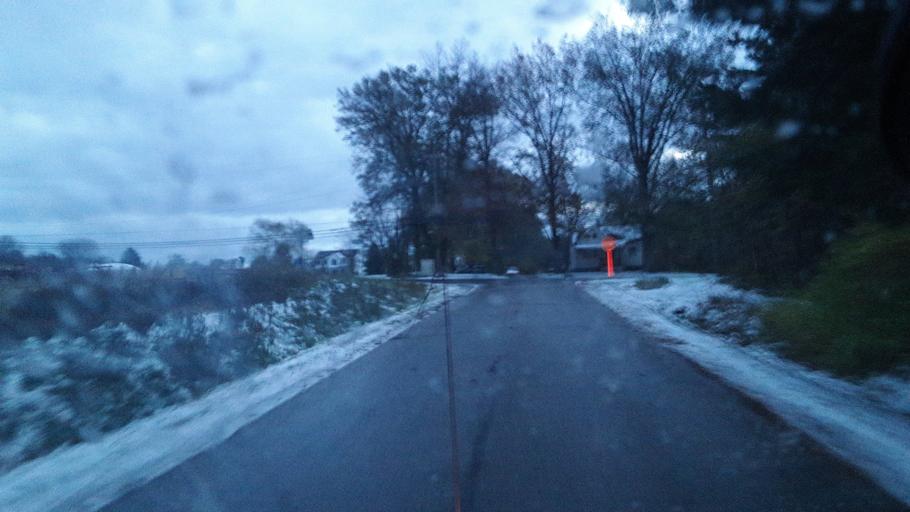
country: US
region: Ohio
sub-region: Portage County
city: Hiram
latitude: 41.3736
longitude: -81.1439
